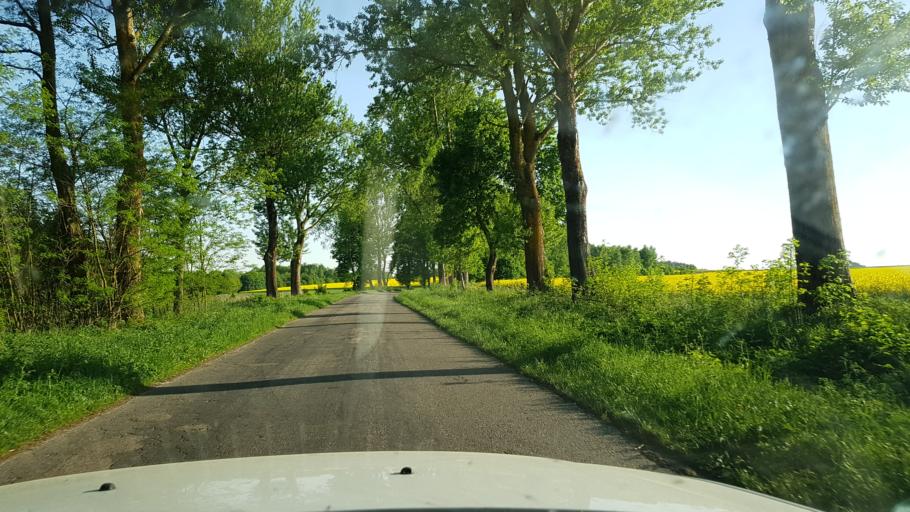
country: PL
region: West Pomeranian Voivodeship
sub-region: Powiat lobeski
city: Dobra
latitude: 53.6294
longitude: 15.3572
